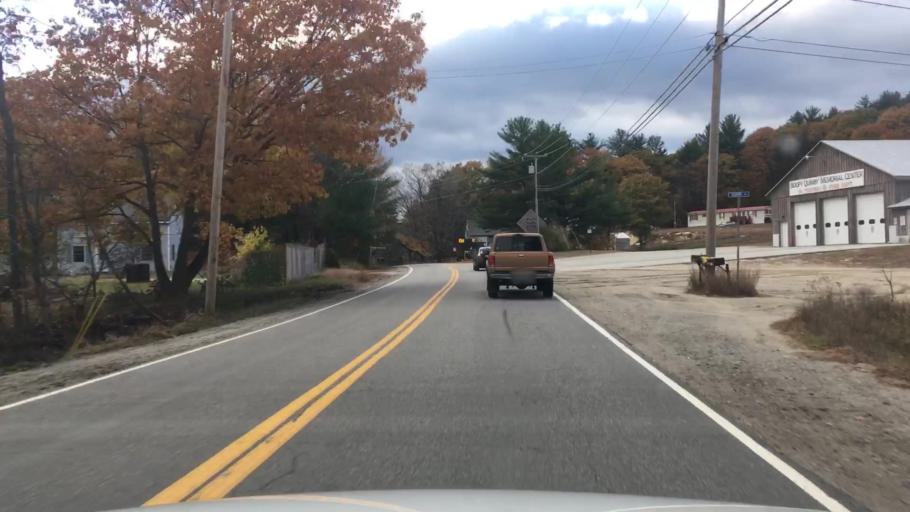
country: US
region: Maine
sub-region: Androscoggin County
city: Livermore
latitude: 44.3405
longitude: -70.2475
